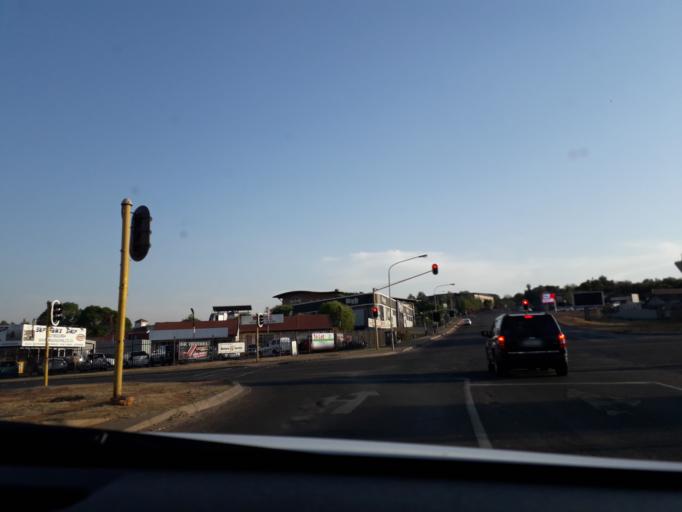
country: ZA
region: Gauteng
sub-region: City of Tshwane Metropolitan Municipality
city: Centurion
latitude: -25.8624
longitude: 28.1905
